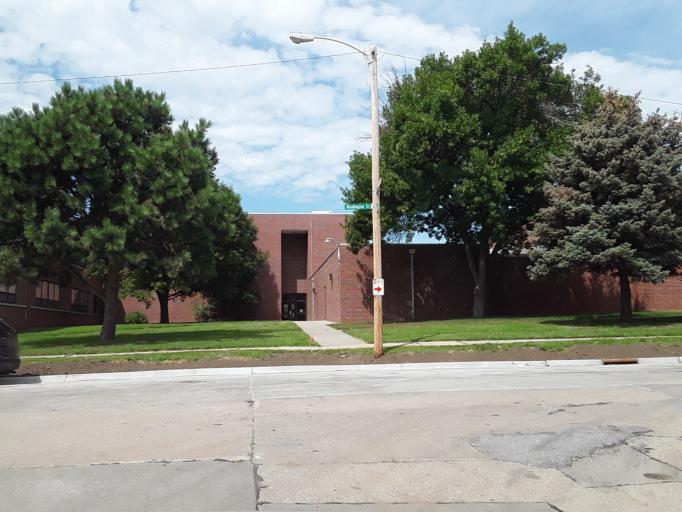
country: US
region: Nebraska
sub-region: Sarpy County
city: Bellevue
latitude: 41.1376
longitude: -95.8962
